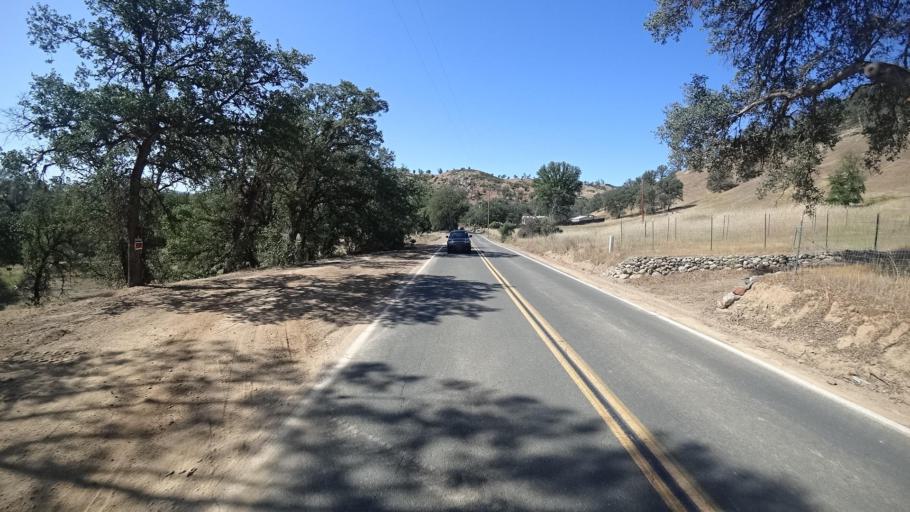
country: US
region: California
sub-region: Lake County
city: Clearlake
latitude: 39.0297
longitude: -122.5768
